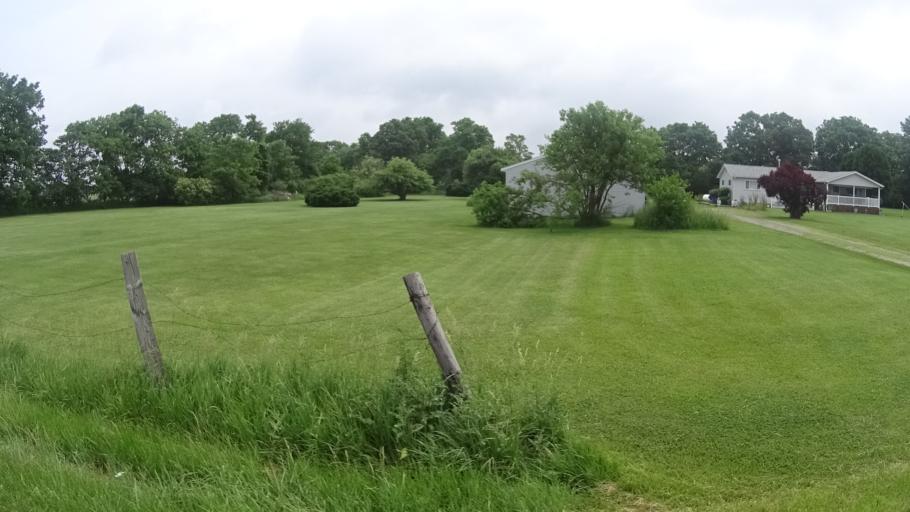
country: US
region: Ohio
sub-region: Erie County
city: Sandusky
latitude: 41.3556
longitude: -82.7558
